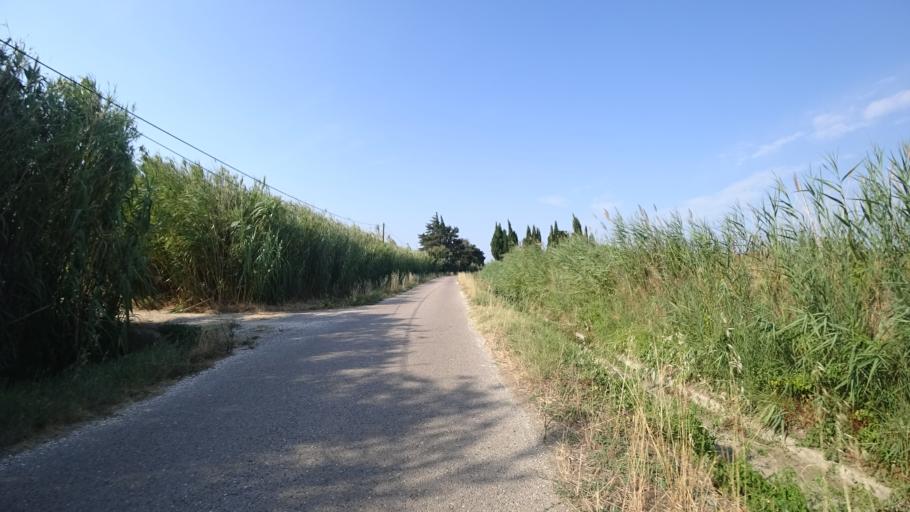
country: FR
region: Languedoc-Roussillon
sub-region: Departement des Pyrenees-Orientales
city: Saint-Laurent-de-la-Salanque
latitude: 42.7837
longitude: 3.0004
